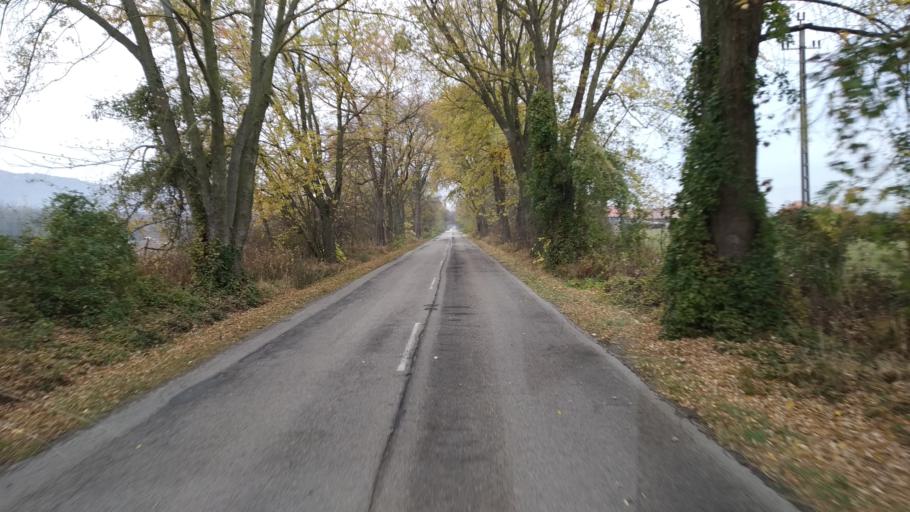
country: HU
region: Pest
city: Dunabogdany
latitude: 47.7987
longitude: 19.0500
